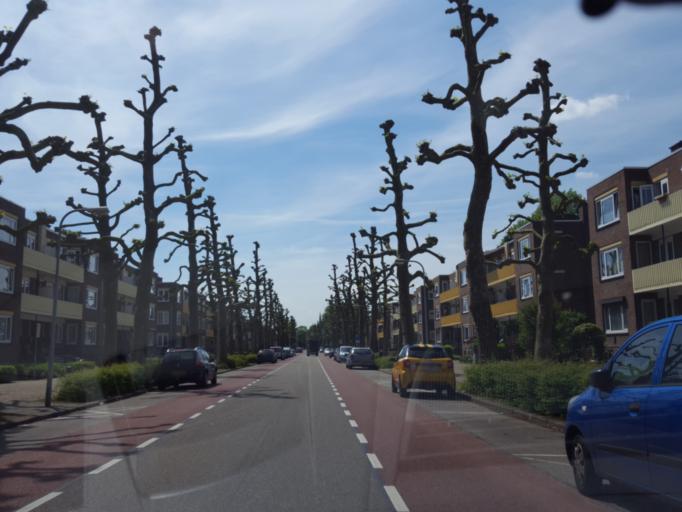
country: NL
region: Limburg
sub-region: Gemeente Weert
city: Weert
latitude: 51.2466
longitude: 5.7021
